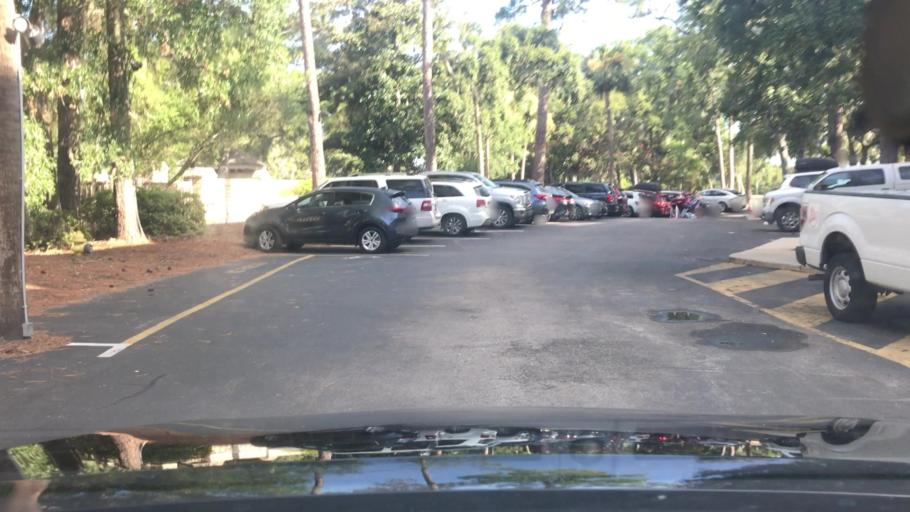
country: US
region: South Carolina
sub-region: Beaufort County
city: Hilton Head Island
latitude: 32.1250
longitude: -80.7885
